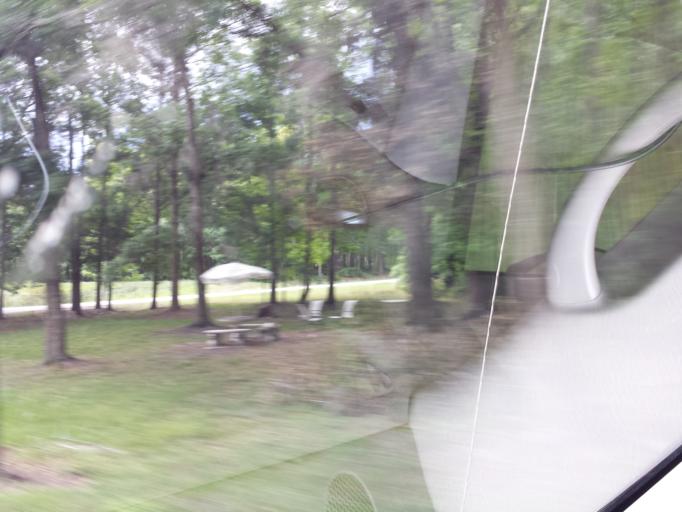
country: US
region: Florida
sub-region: Hernando County
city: Brooksville
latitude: 28.5566
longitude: -82.3756
